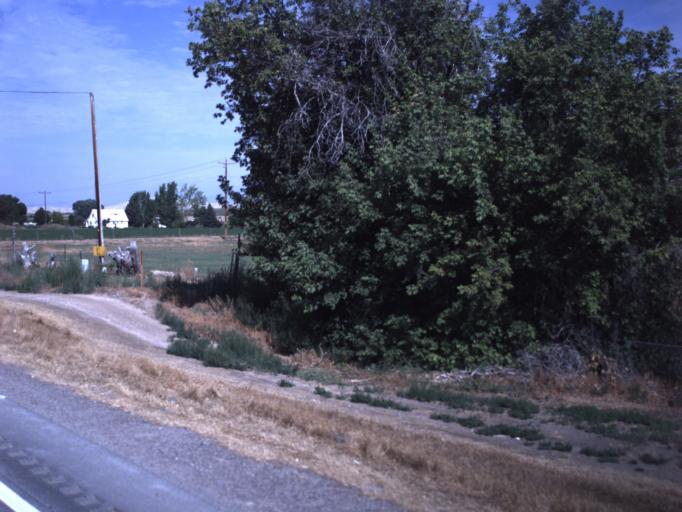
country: US
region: Utah
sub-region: Uintah County
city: Naples
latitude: 40.3698
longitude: -109.3501
